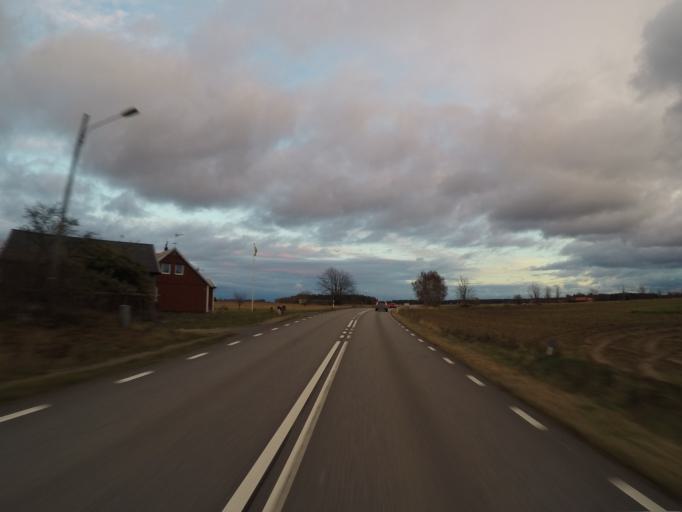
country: SE
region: Skane
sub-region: Kristianstads Kommun
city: Degeberga
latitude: 55.8961
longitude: 14.0772
